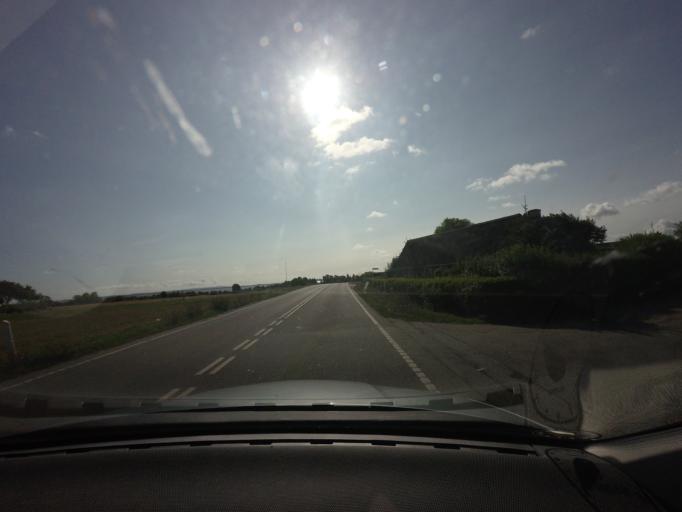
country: DK
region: Zealand
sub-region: Vordingborg Kommune
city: Stege
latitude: 55.0028
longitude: 12.1539
